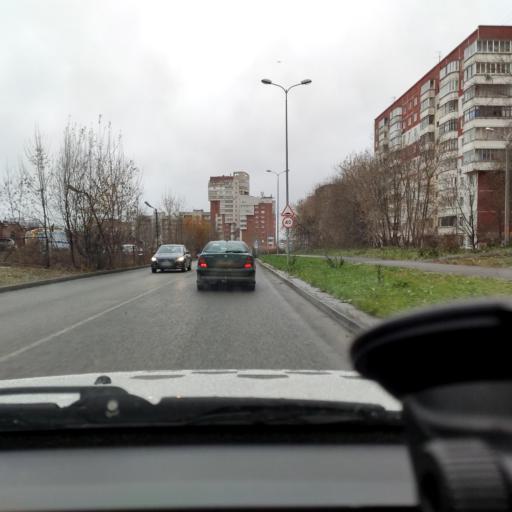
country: RU
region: Perm
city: Perm
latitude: 58.0055
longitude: 56.2980
